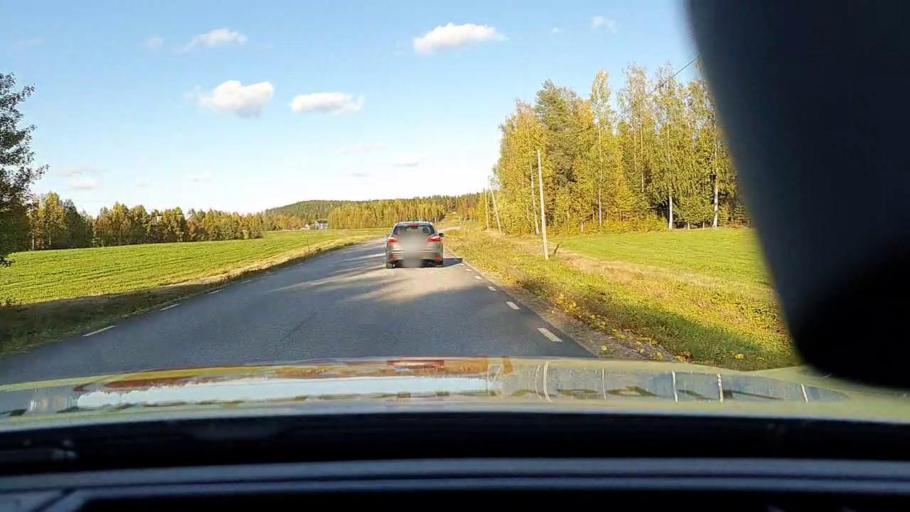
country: SE
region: Norrbotten
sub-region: Pitea Kommun
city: Norrfjarden
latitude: 65.5109
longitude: 21.4900
